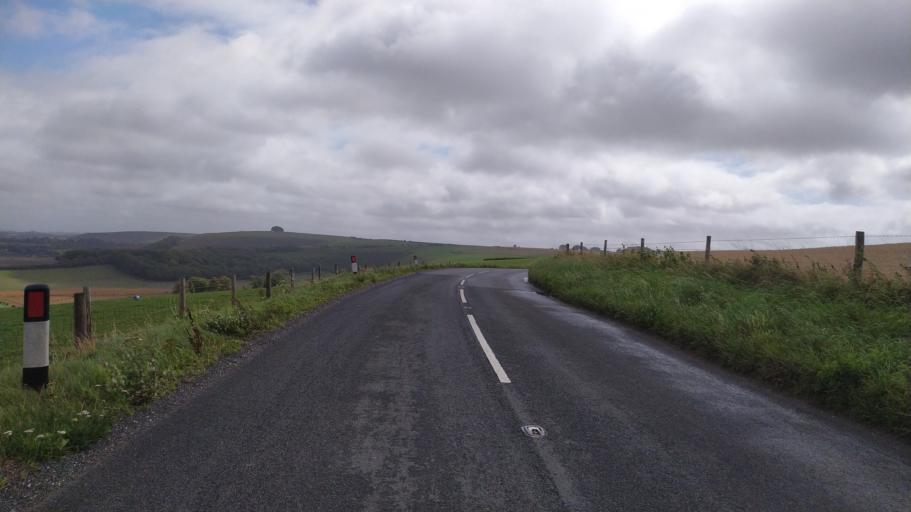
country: GB
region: England
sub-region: Dorset
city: Shaftesbury
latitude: 50.9856
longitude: -2.1429
